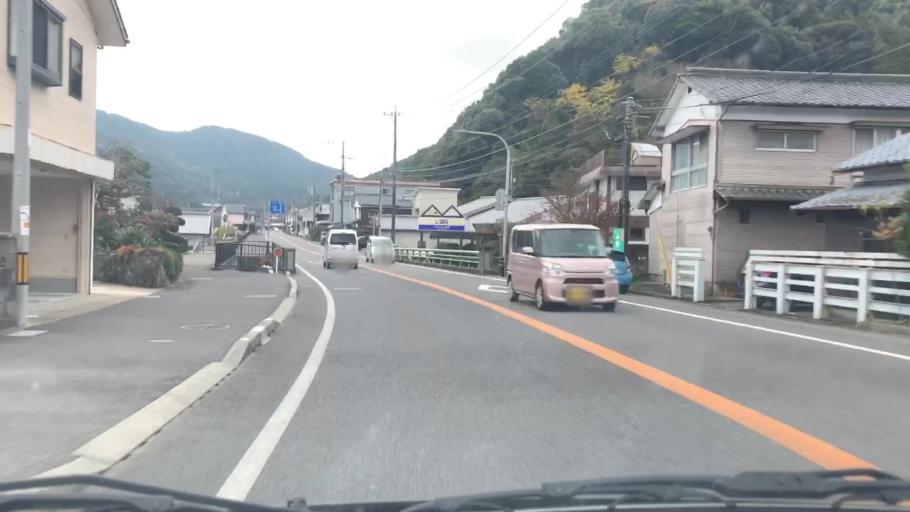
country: JP
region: Saga Prefecture
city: Ureshinomachi-shimojuku
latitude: 33.0939
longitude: 129.9770
